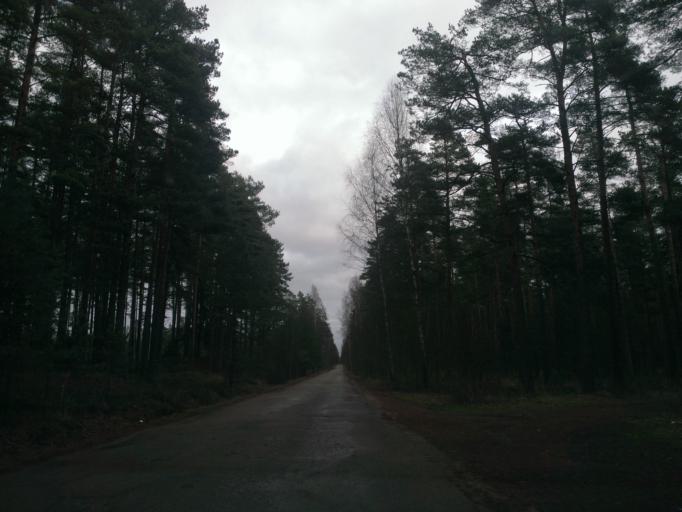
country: LV
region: Riga
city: Bergi
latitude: 57.0046
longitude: 24.3133
